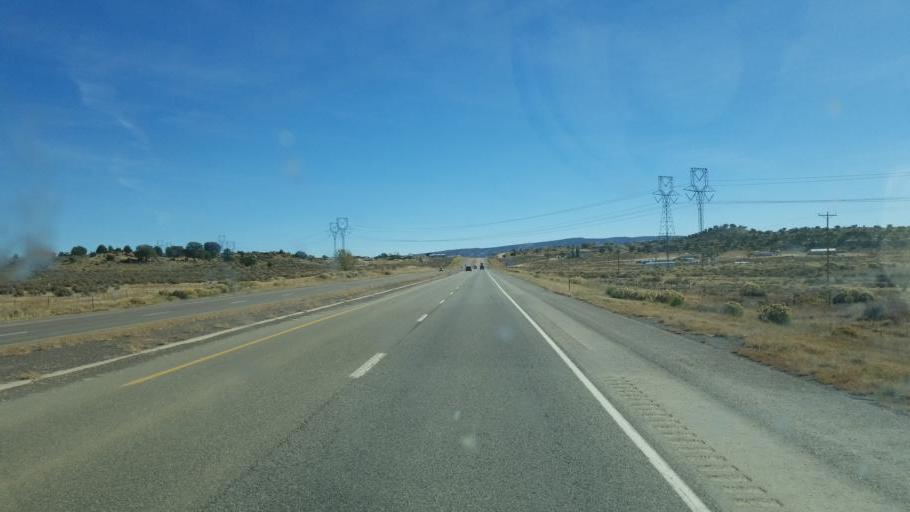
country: US
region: New Mexico
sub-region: McKinley County
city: Twin Lakes
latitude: 35.6325
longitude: -108.8050
